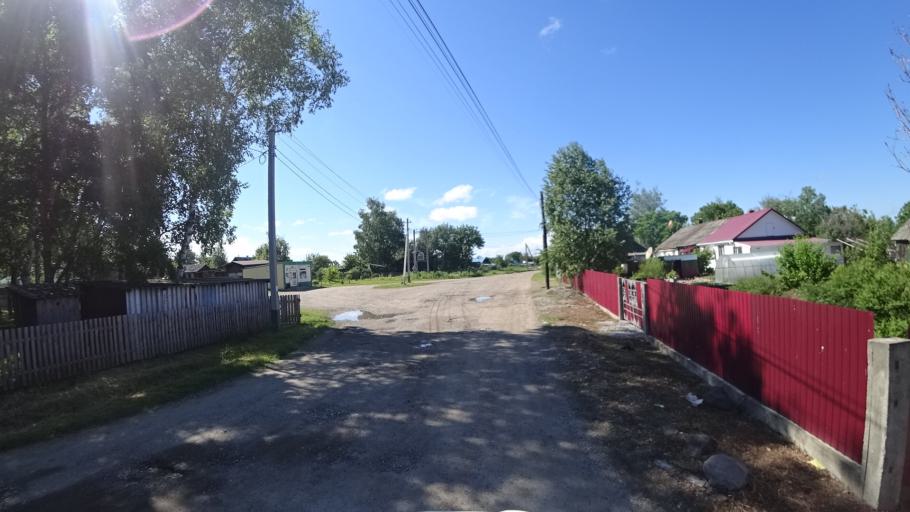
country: RU
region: Khabarovsk Krai
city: Khor
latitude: 47.8876
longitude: 135.0356
